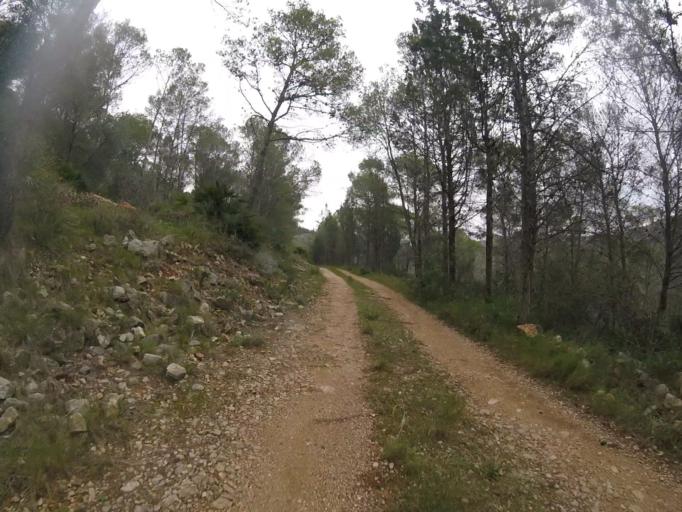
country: ES
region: Valencia
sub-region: Provincia de Castello
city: Santa Magdalena de Pulpis
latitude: 40.3185
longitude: 0.2804
